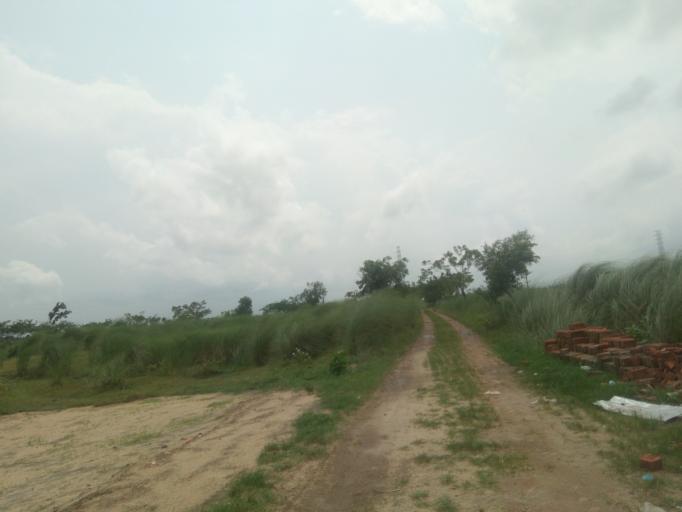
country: BD
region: Dhaka
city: Azimpur
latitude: 23.7507
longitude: 90.3374
